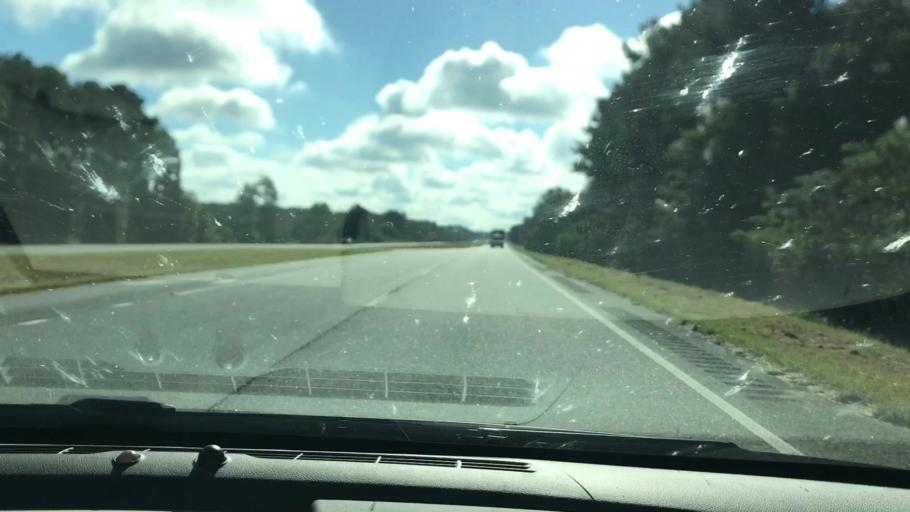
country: US
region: Georgia
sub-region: Worth County
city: Sylvester
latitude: 31.5543
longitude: -83.9876
